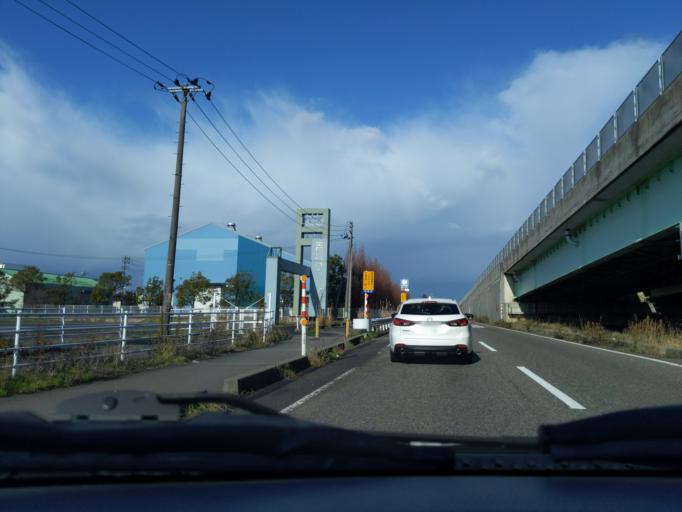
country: JP
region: Niigata
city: Kameda-honcho
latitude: 37.8702
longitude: 139.0873
